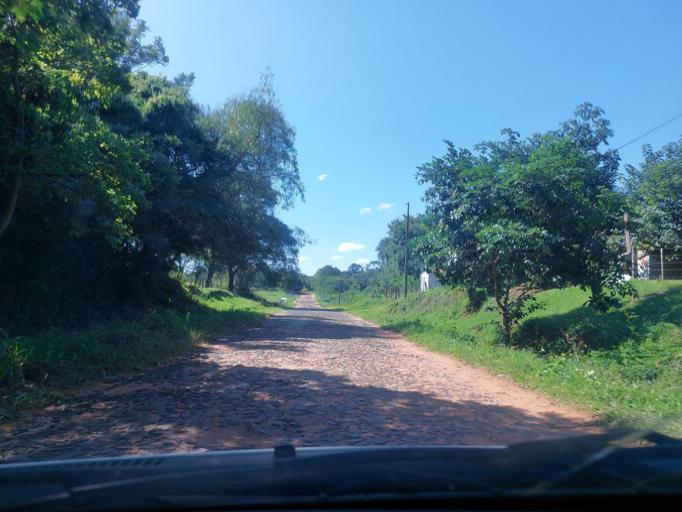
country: PY
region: San Pedro
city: Itacurubi del Rosario
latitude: -24.5688
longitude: -56.5955
